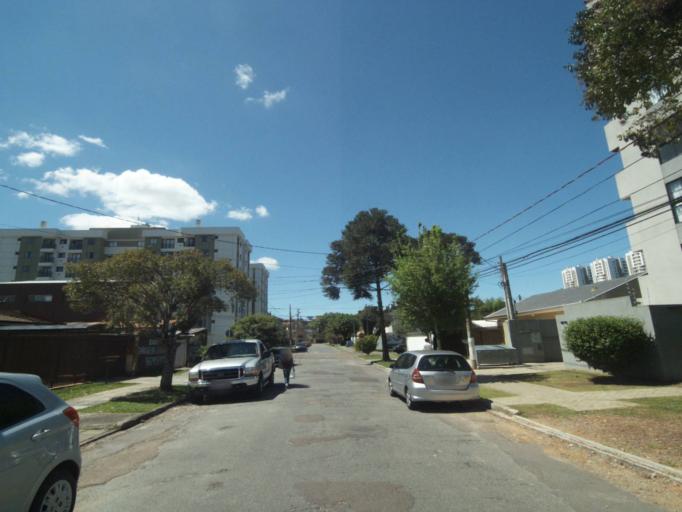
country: BR
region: Parana
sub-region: Curitiba
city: Curitiba
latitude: -25.3885
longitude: -49.2402
